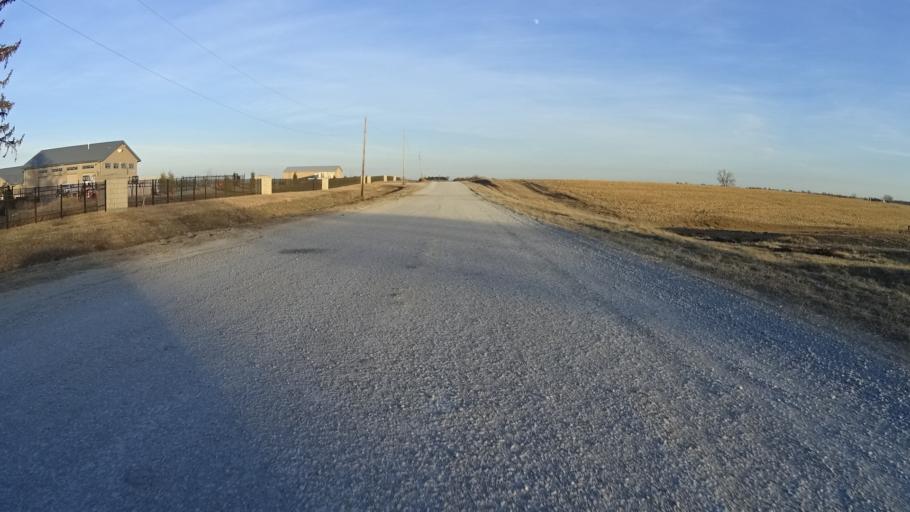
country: US
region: Nebraska
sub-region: Sarpy County
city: Springfield
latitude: 41.1325
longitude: -96.1299
